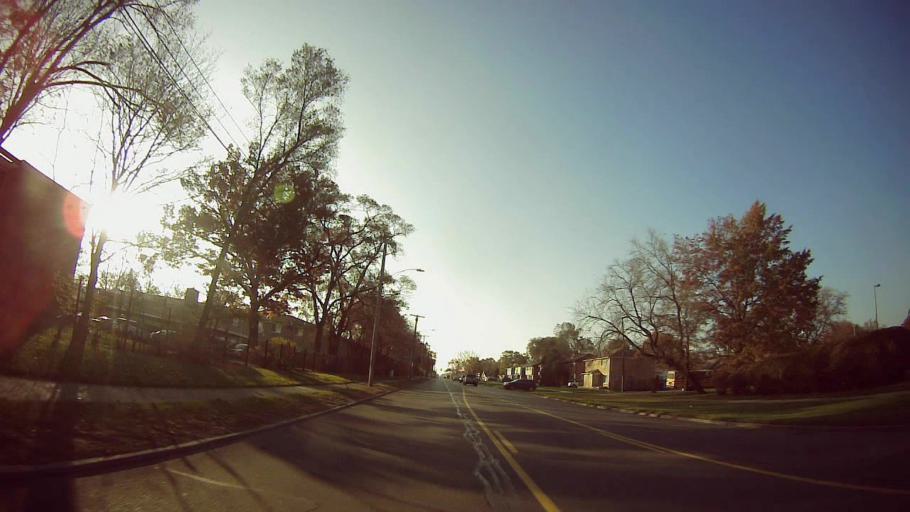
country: US
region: Michigan
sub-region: Oakland County
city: Oak Park
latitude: 42.4373
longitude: -83.1611
